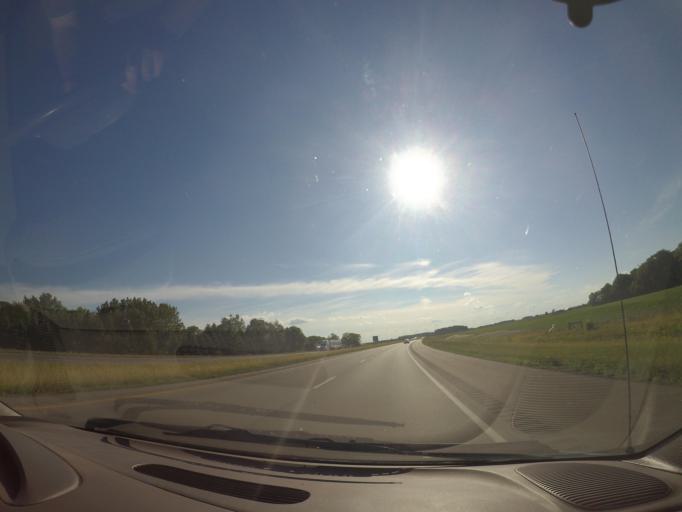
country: US
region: Ohio
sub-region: Henry County
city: Liberty Center
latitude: 41.4157
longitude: -84.0458
